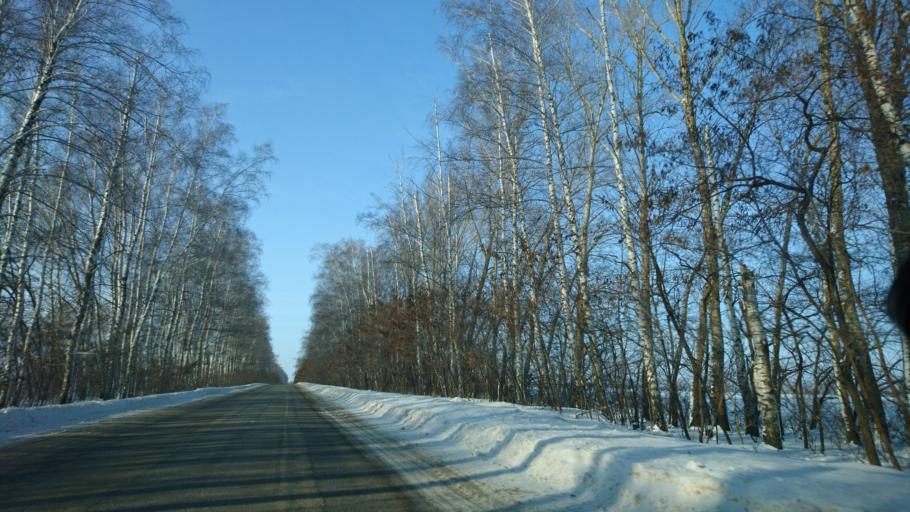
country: RU
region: Belgorod
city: Severnyy
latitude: 50.7280
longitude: 36.5476
